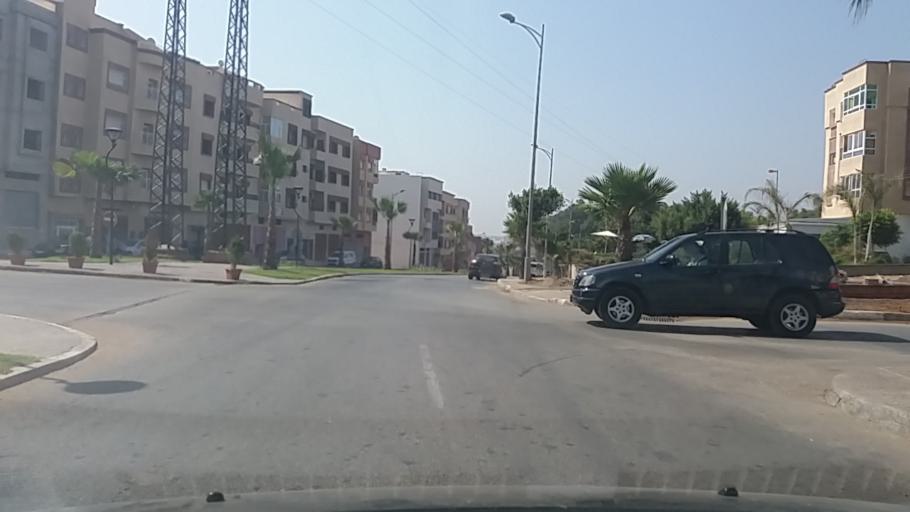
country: MA
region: Gharb-Chrarda-Beni Hssen
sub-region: Kenitra Province
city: Kenitra
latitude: 34.2526
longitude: -6.6149
